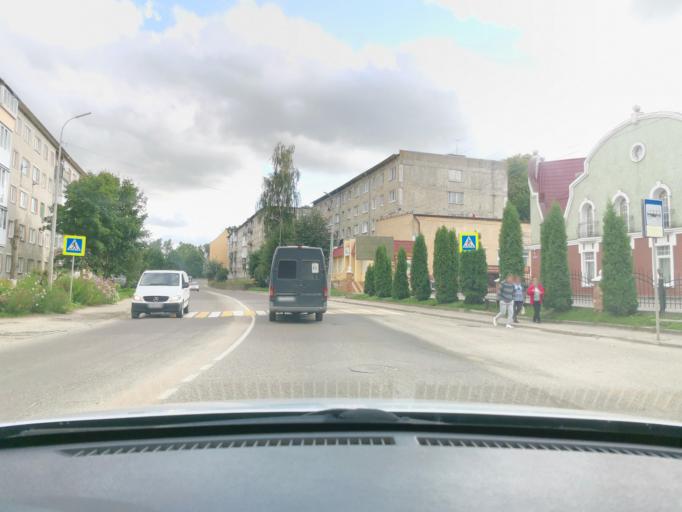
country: RU
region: Kaliningrad
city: Chernyakhovsk
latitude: 54.6418
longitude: 21.8075
